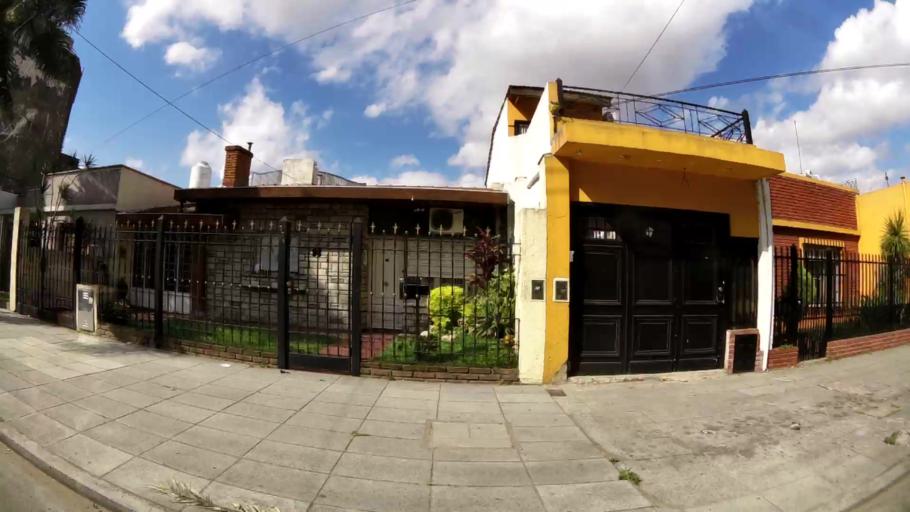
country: AR
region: Buenos Aires
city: San Justo
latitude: -34.6513
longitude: -58.5750
